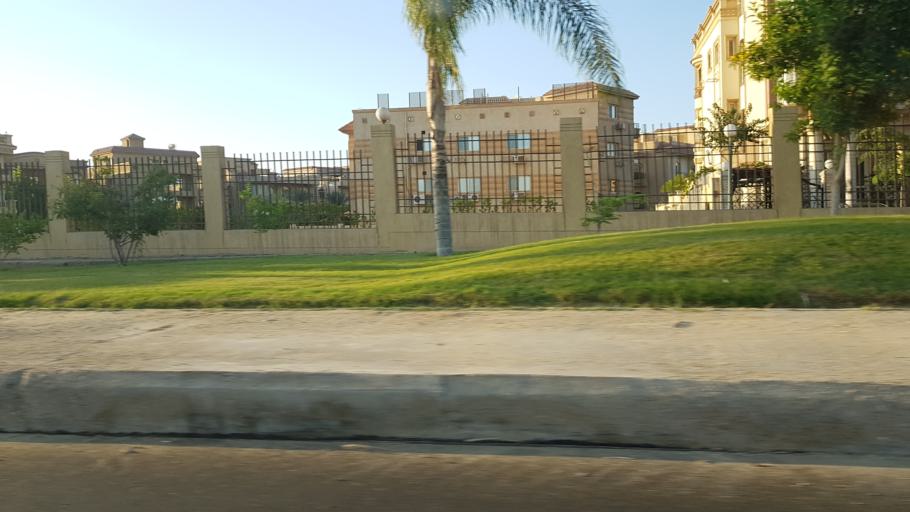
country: EG
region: Muhafazat al Qalyubiyah
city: Al Khankah
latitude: 30.0620
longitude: 31.4393
